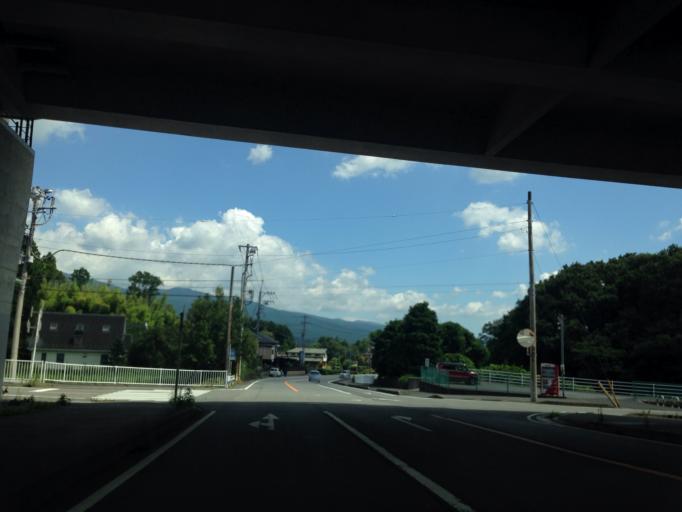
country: JP
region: Shizuoka
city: Gotemba
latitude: 35.2215
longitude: 138.8884
